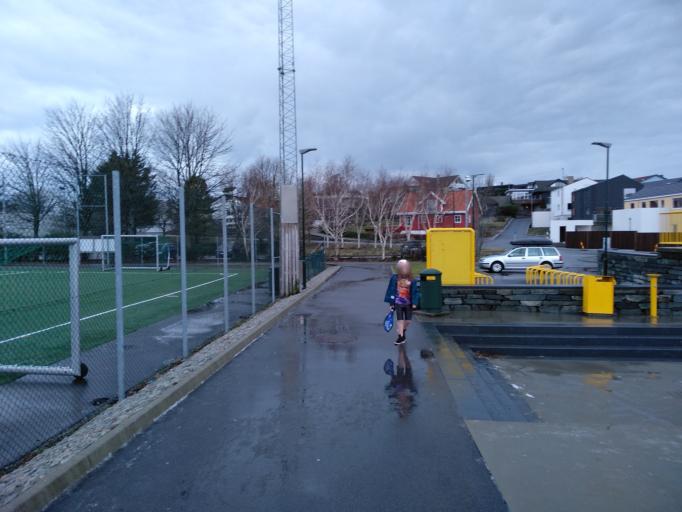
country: NO
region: Rogaland
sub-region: Stavanger
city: Stavanger
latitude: 58.9896
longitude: 5.6882
